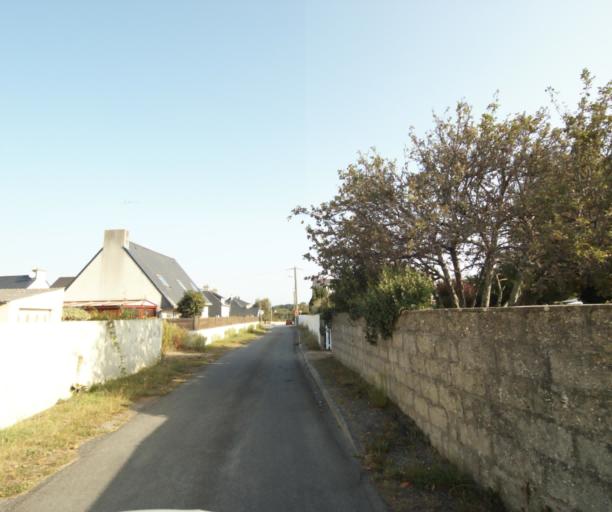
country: FR
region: Brittany
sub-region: Departement du Morbihan
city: Riantec
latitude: 47.7091
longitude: -3.3187
